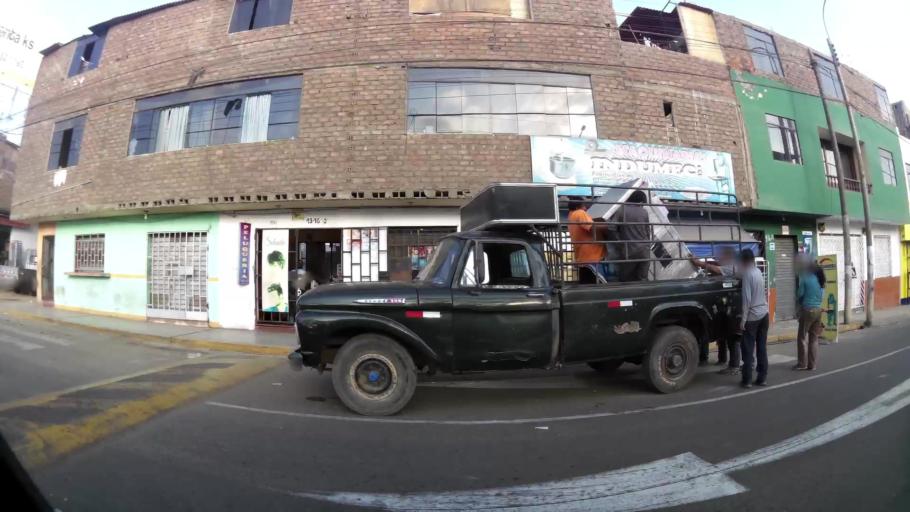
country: PE
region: La Libertad
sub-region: Provincia de Trujillo
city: El Porvenir
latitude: -8.0990
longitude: -79.0136
